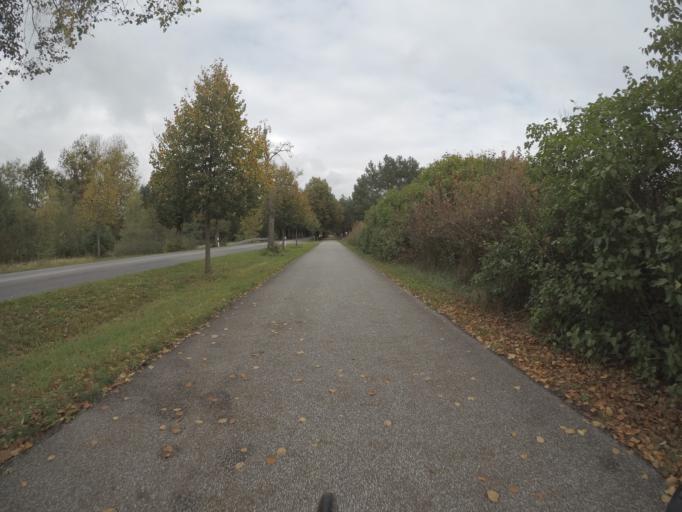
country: DE
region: Berlin
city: Buch
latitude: 52.6708
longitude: 13.4977
